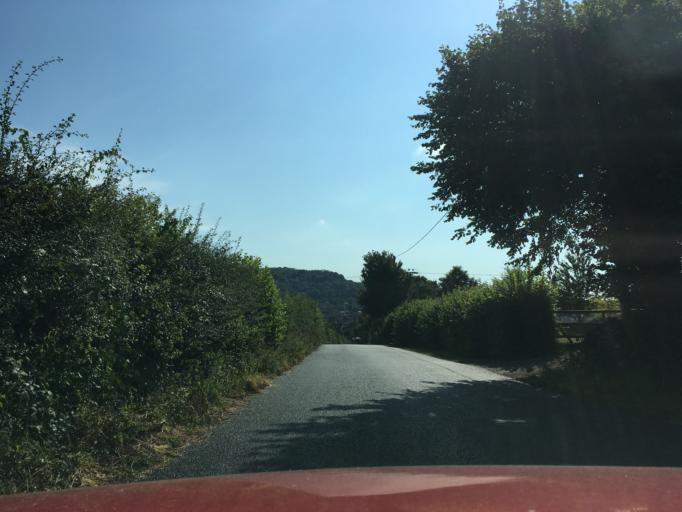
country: GB
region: England
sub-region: Gloucestershire
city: Dursley
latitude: 51.7015
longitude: -2.3547
